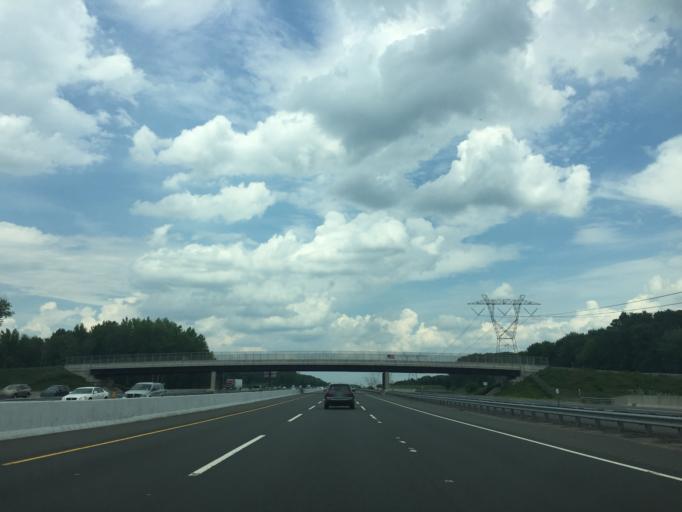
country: US
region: New Jersey
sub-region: Monmouth County
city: Allentown
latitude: 40.2198
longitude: -74.5627
